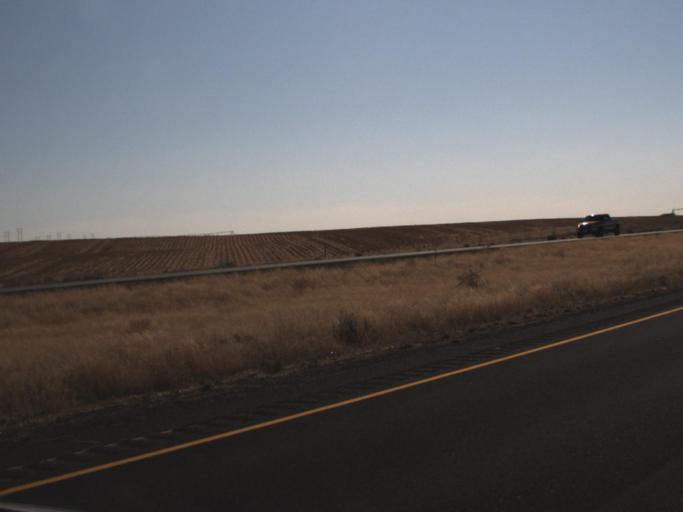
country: US
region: Washington
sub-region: Franklin County
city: Pasco
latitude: 46.3059
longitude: -119.0936
